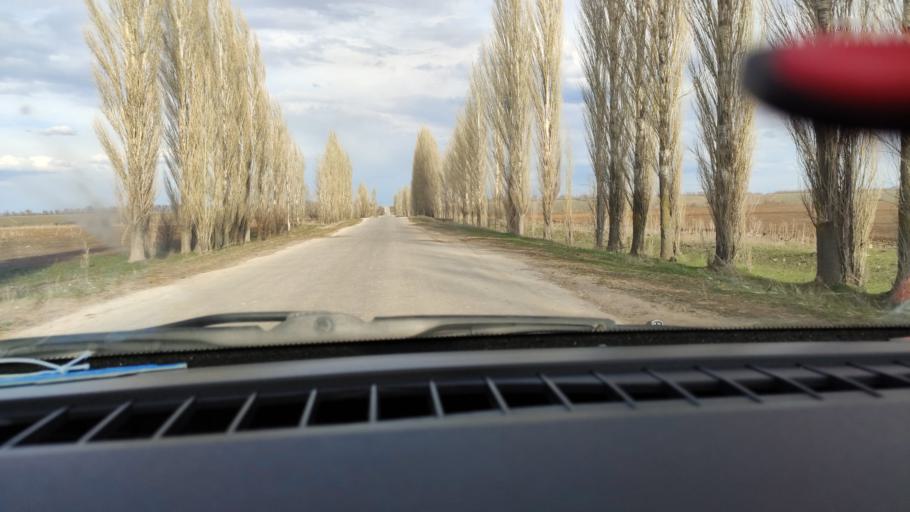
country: RU
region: Saratov
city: Rovnoye
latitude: 50.9386
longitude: 46.1074
